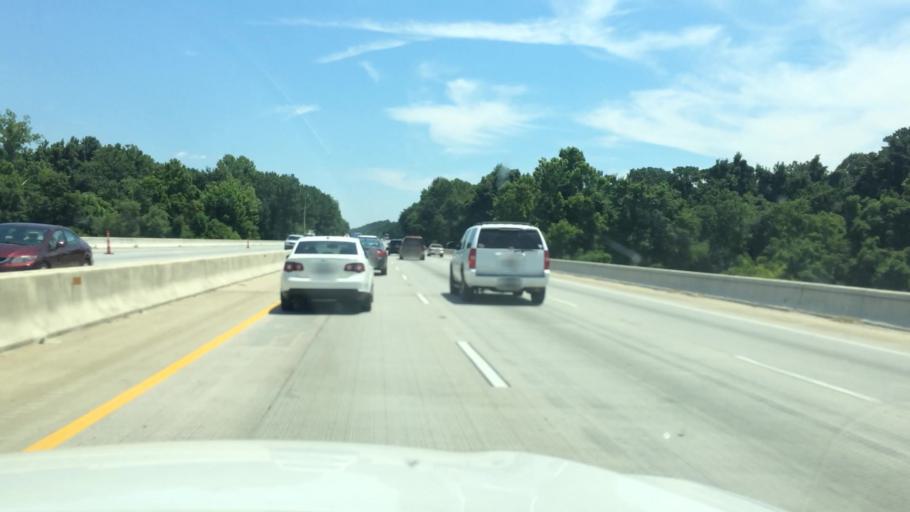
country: US
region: South Carolina
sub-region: Lexington County
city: West Columbia
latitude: 34.0477
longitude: -81.0737
